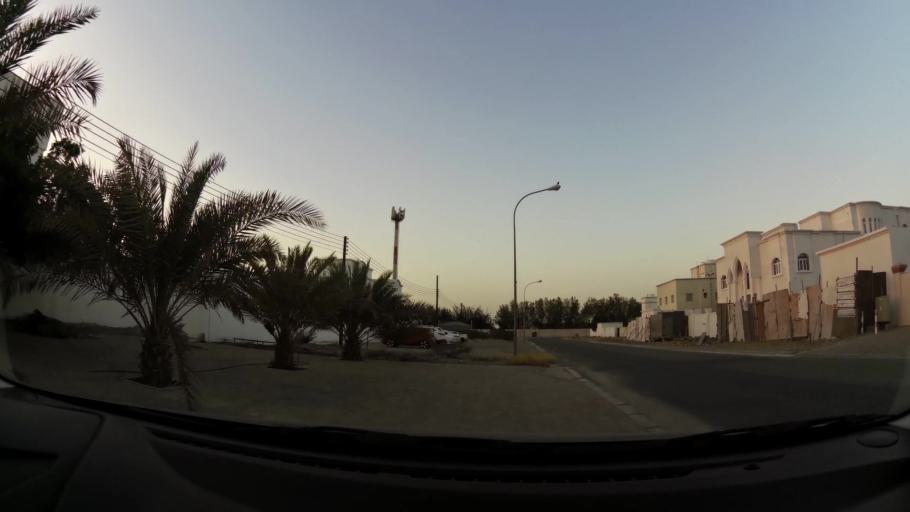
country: OM
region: Muhafazat Masqat
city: As Sib al Jadidah
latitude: 23.6466
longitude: 58.2092
